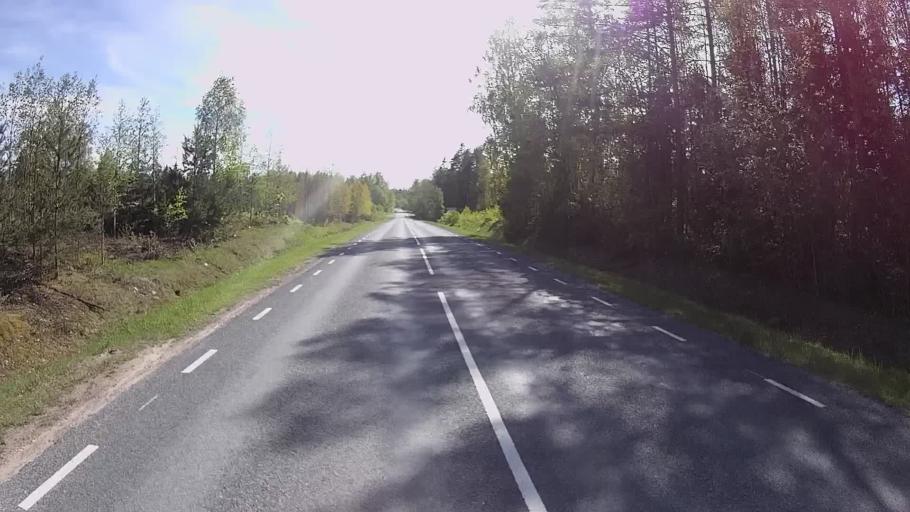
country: EE
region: Vorumaa
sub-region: Antsla vald
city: Vana-Antsla
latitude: 57.9834
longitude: 26.4734
